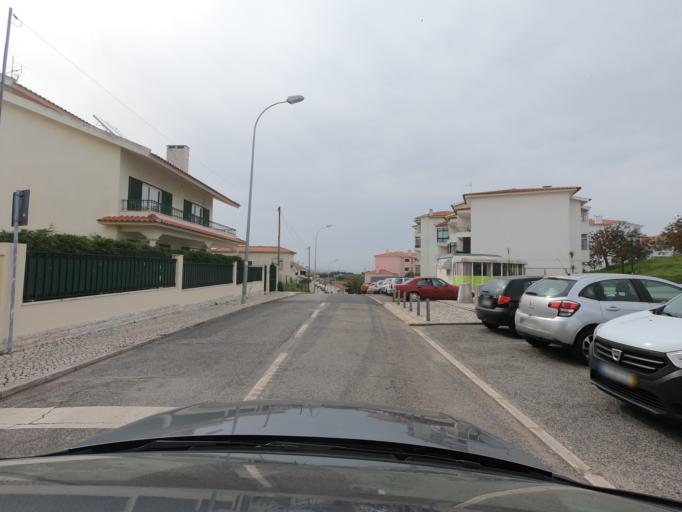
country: PT
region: Lisbon
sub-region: Oeiras
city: Porto Salvo
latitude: 38.7196
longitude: -9.2932
